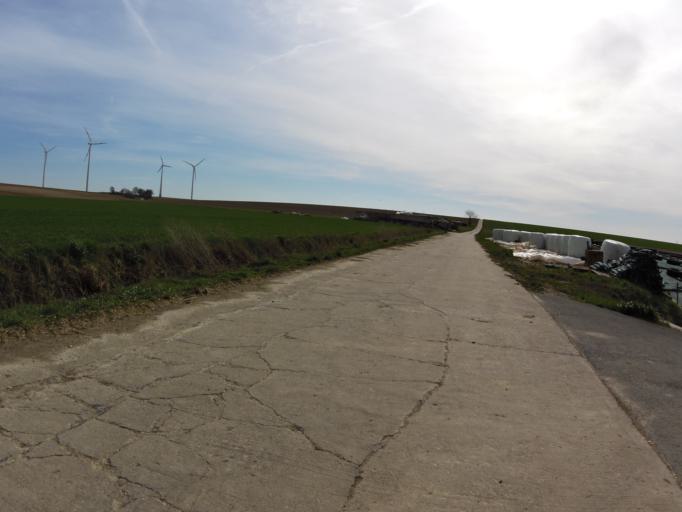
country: DE
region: Bavaria
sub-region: Regierungsbezirk Unterfranken
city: Biebelried
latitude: 49.7621
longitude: 10.0845
